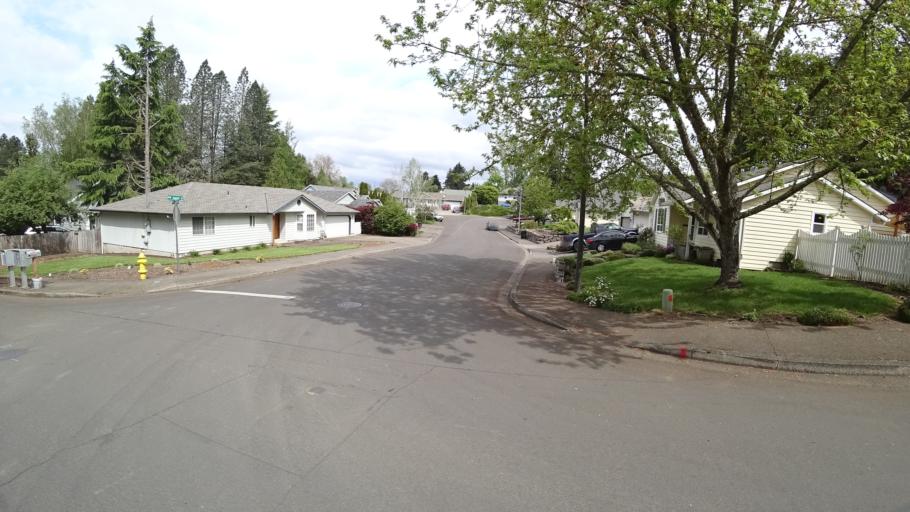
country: US
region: Oregon
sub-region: Washington County
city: Hillsboro
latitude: 45.5253
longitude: -123.0002
